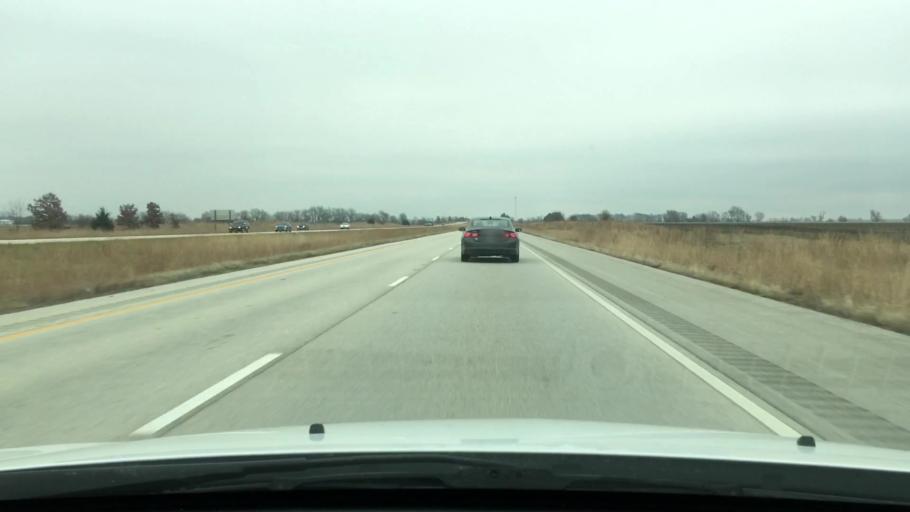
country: US
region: Illinois
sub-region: Sangamon County
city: New Berlin
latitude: 39.7403
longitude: -89.8959
